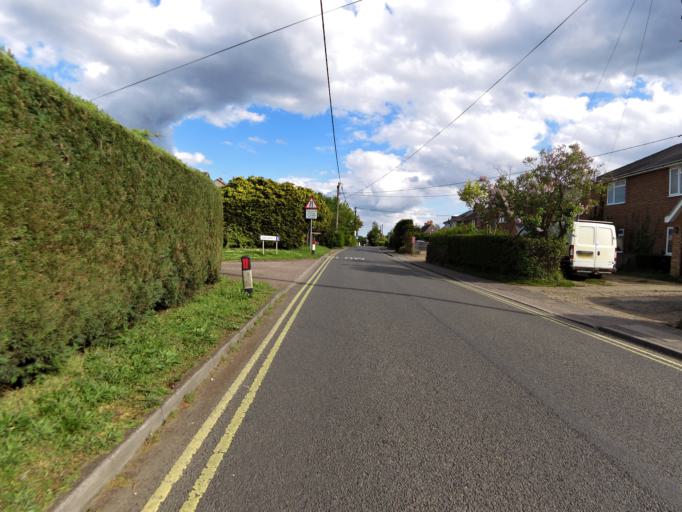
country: GB
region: England
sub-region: Suffolk
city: Woolpit
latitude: 52.2224
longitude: 0.8943
